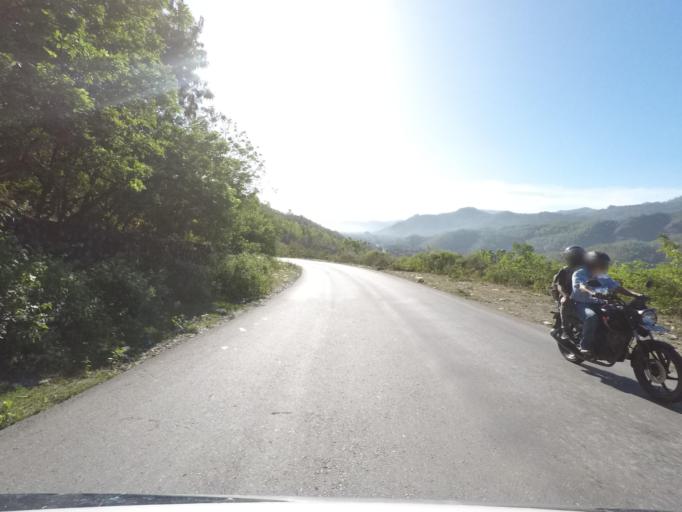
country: TL
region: Dili
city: Dili
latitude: -8.5585
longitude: 125.6415
